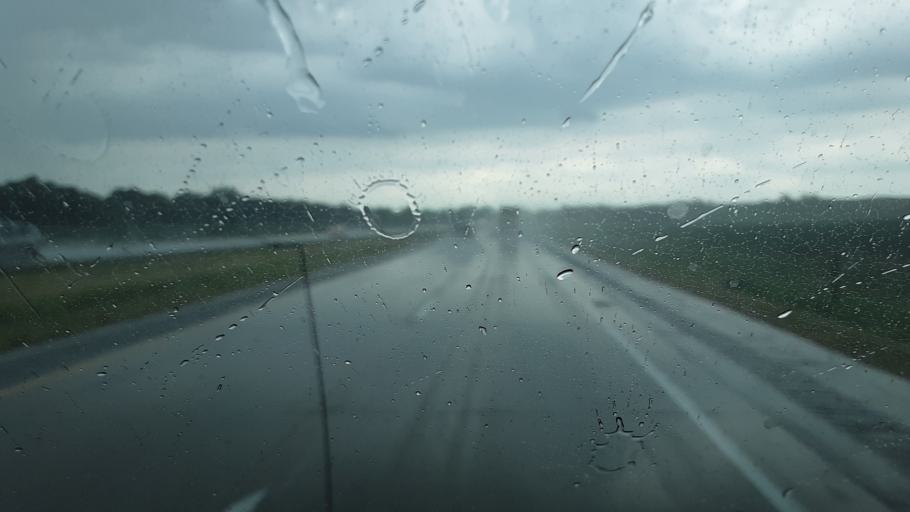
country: US
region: Iowa
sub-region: Pottawattamie County
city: Council Bluffs
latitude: 41.3044
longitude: -95.7681
